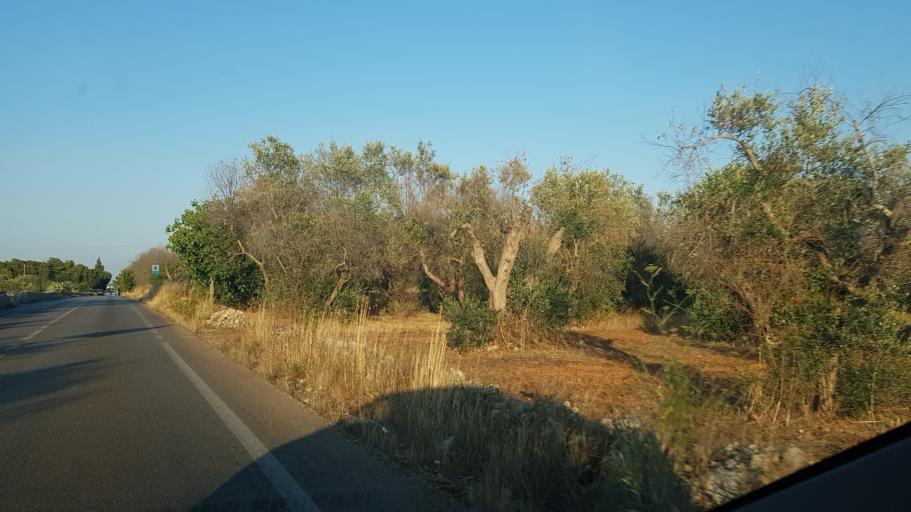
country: IT
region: Apulia
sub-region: Provincia di Lecce
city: Ruffano
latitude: 39.9625
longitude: 18.2715
